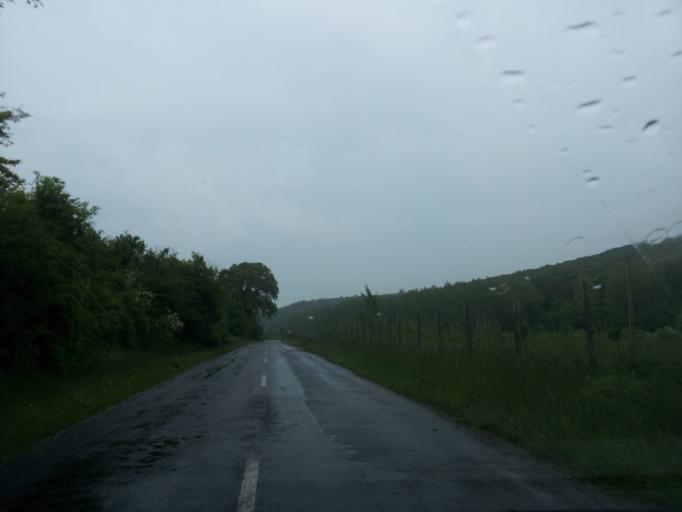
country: HU
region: Tolna
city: Szekszard
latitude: 46.2832
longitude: 18.6475
